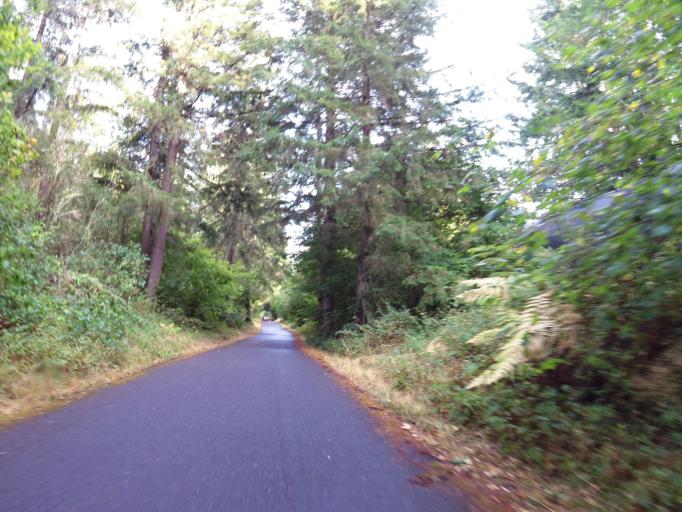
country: US
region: Washington
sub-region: Thurston County
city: Rainier
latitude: 46.9040
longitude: -122.7673
